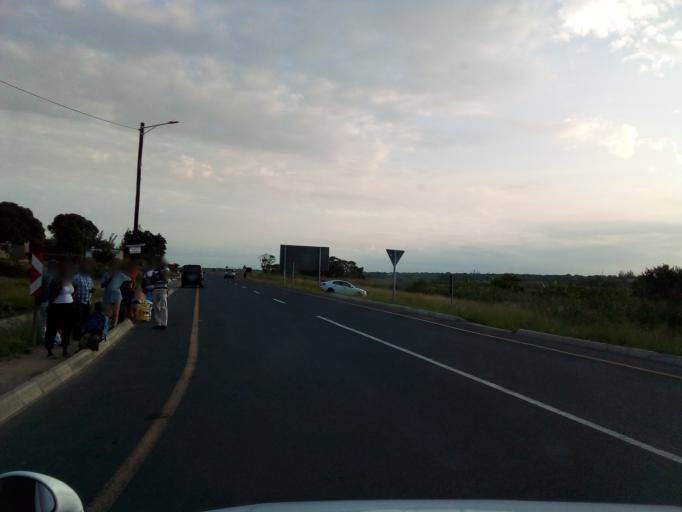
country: MZ
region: Maputo City
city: Maputo
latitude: -26.0063
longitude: 32.5574
